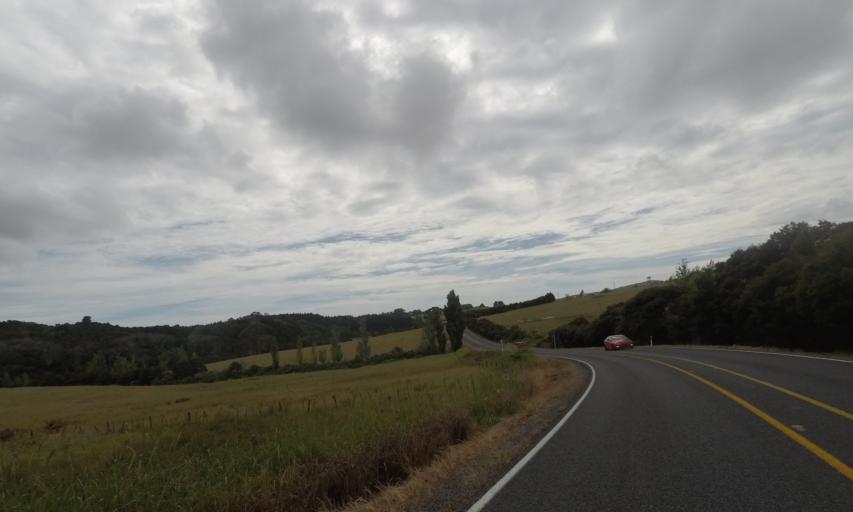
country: NZ
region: Northland
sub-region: Whangarei
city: Ruakaka
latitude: -35.7691
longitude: 174.4844
